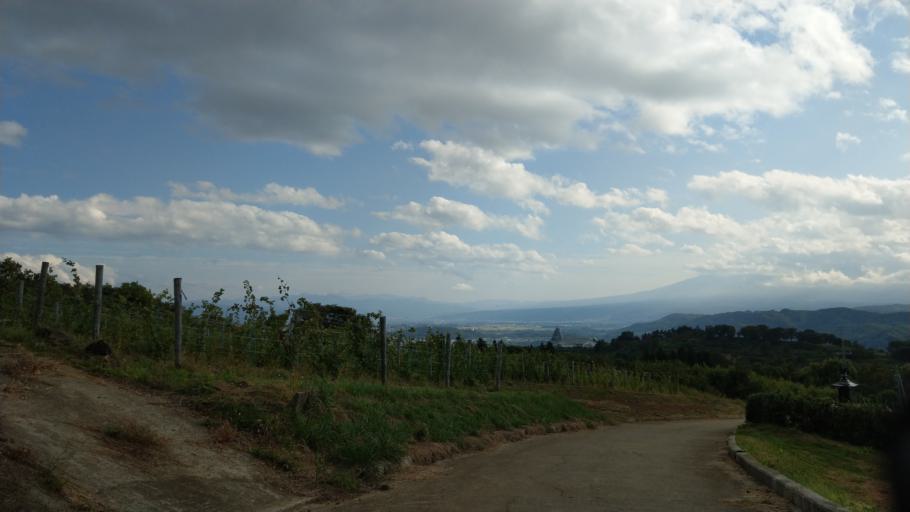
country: JP
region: Nagano
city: Komoro
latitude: 36.3524
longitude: 138.4193
